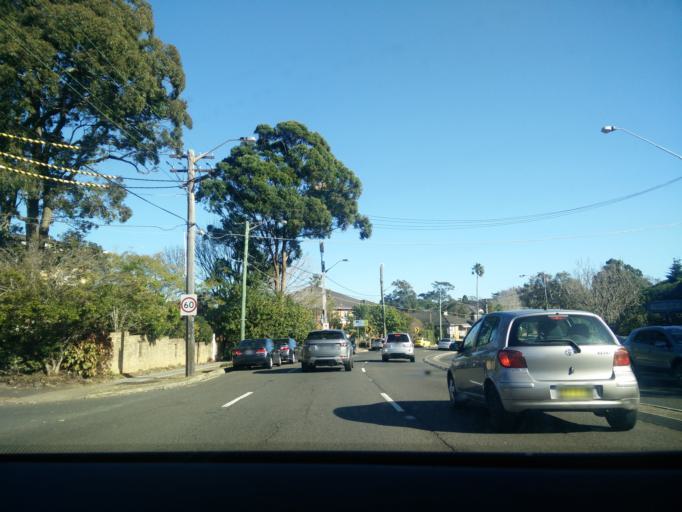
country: AU
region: New South Wales
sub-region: Ku-ring-gai
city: Lindfield
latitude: -33.7830
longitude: 151.1727
